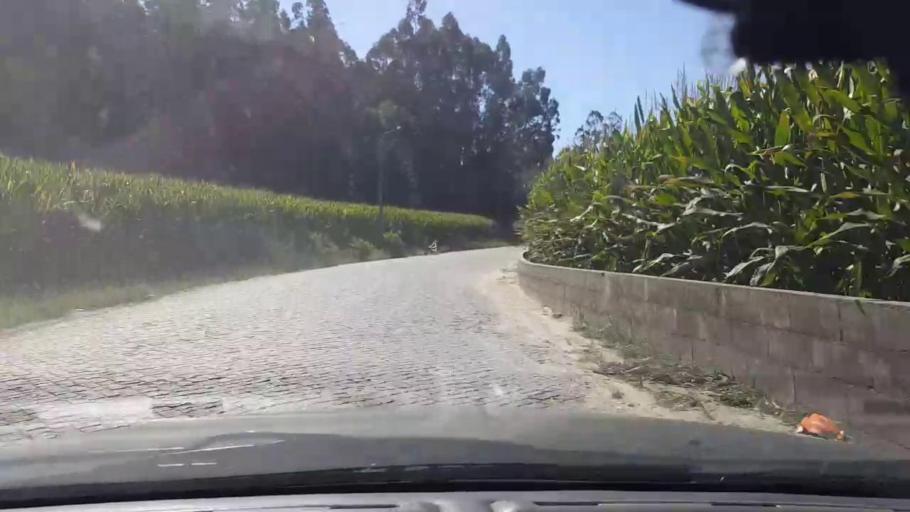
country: PT
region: Porto
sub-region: Maia
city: Gemunde
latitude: 41.2946
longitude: -8.6659
